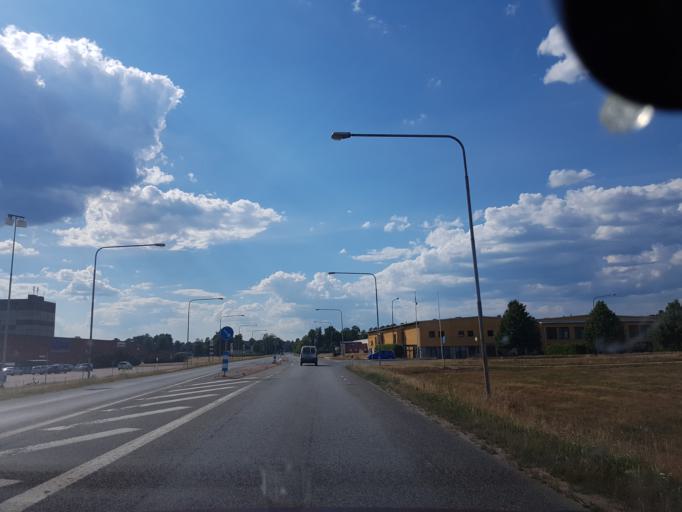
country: SE
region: Joenkoeping
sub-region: Gislaveds Kommun
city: Gislaved
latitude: 57.2963
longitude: 13.5665
